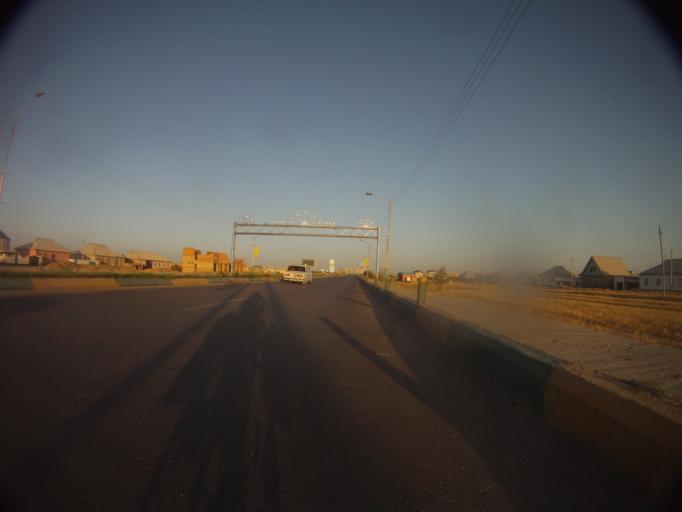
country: KZ
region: Ongtustik Qazaqstan
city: Turkestan
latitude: 43.2795
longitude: 68.3234
